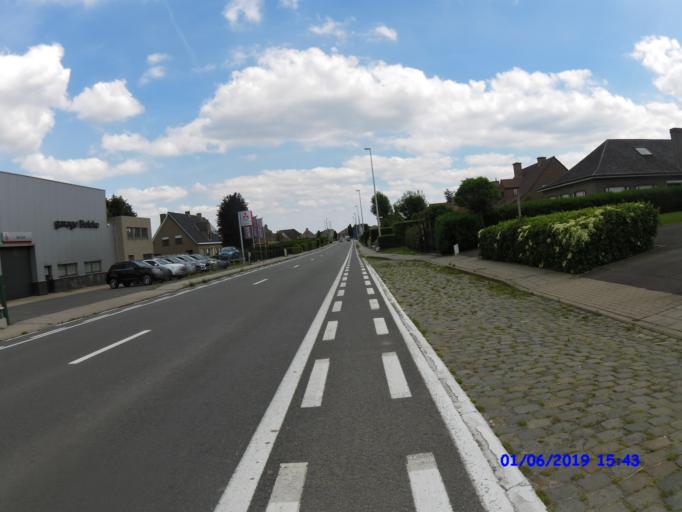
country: BE
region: Flanders
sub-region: Provincie West-Vlaanderen
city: Diksmuide
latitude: 51.0289
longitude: 2.8866
